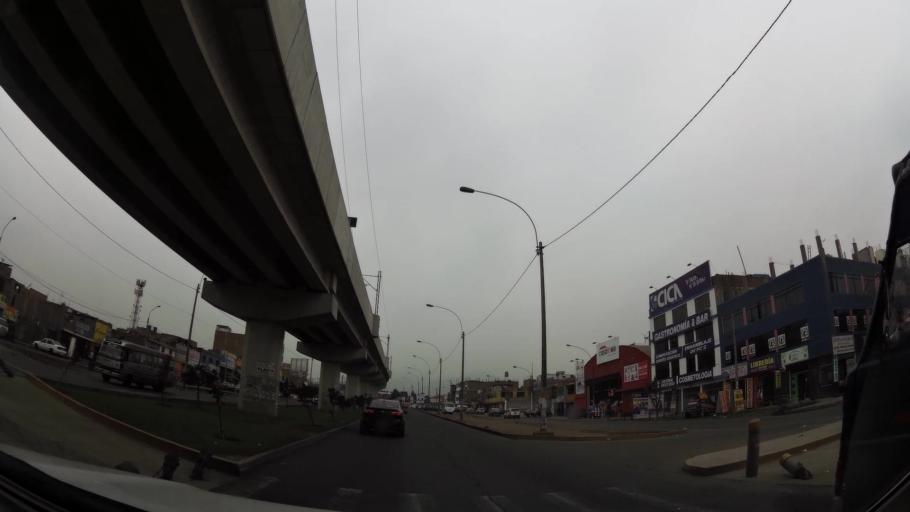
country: PE
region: Lima
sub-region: Lima
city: Independencia
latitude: -11.9734
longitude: -76.9981
